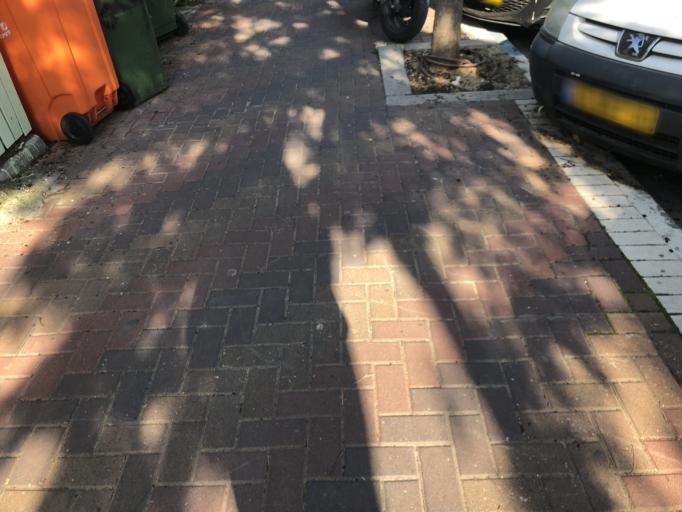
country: IL
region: Tel Aviv
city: Giv`atayim
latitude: 32.0717
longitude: 34.8124
